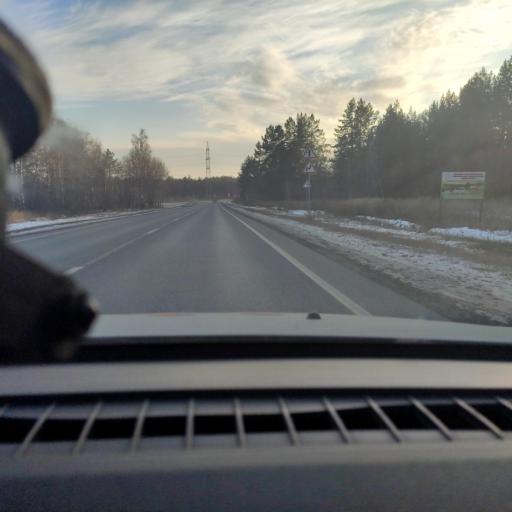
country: RU
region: Samara
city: Volzhskiy
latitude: 53.4537
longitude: 50.1261
